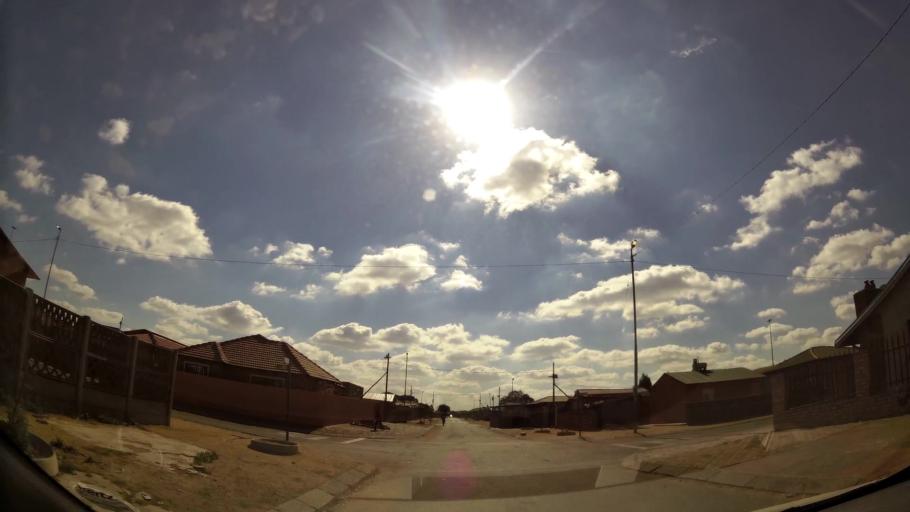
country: ZA
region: Gauteng
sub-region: West Rand District Municipality
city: Krugersdorp
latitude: -26.1417
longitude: 27.7964
